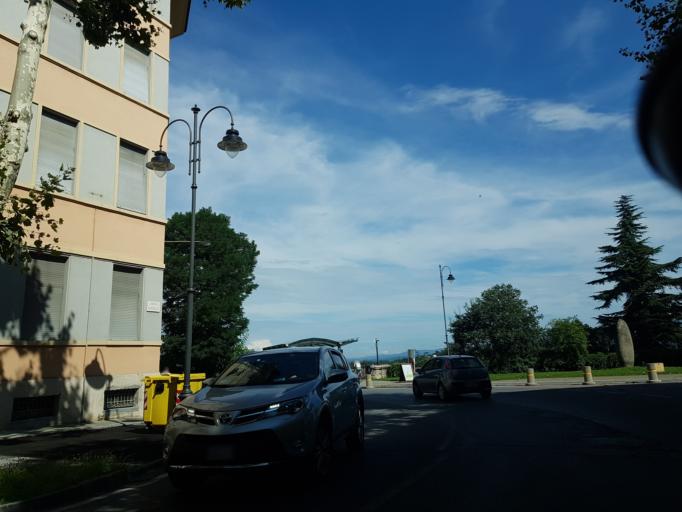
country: IT
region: Piedmont
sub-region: Provincia di Cuneo
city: Cuneo
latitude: 44.3874
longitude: 7.5498
